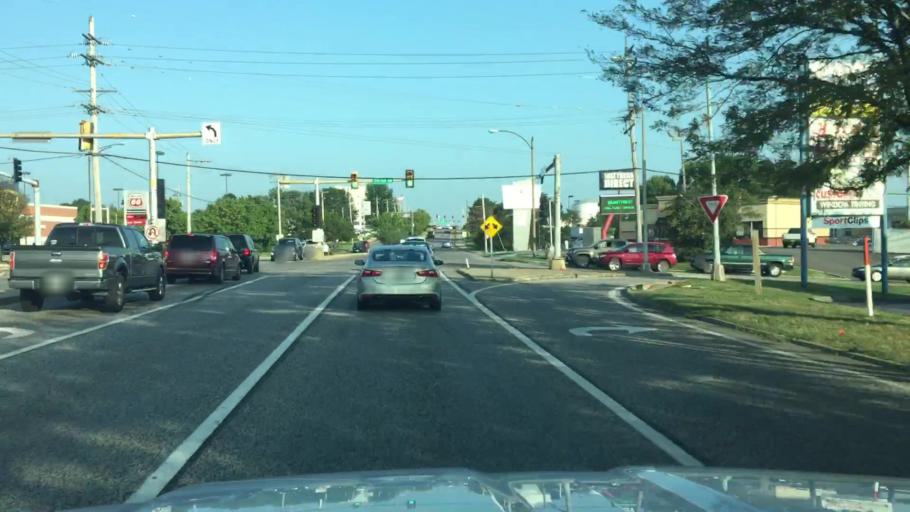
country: US
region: Missouri
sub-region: Saint Louis County
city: Mehlville
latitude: 38.5097
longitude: -90.3326
